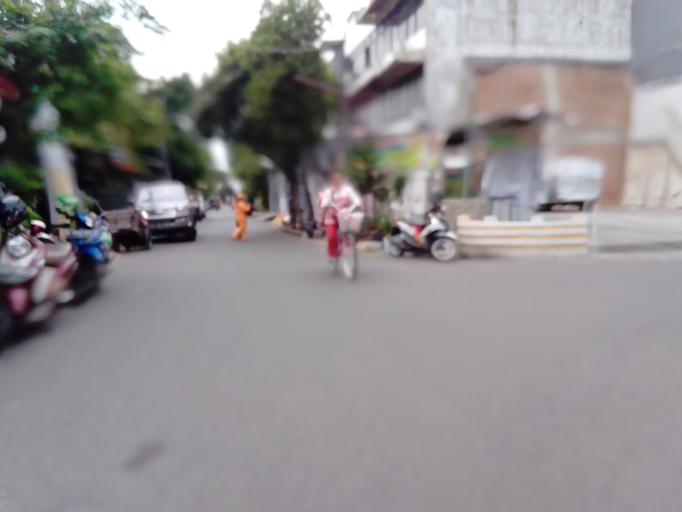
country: ID
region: Jakarta Raya
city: Jakarta
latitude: -6.1567
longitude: 106.8147
